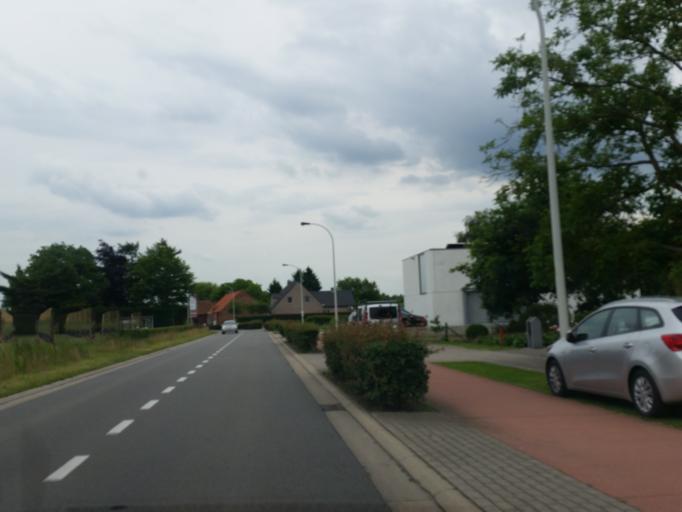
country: BE
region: Flanders
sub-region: Provincie Antwerpen
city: Lier
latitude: 51.1624
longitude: 4.5925
